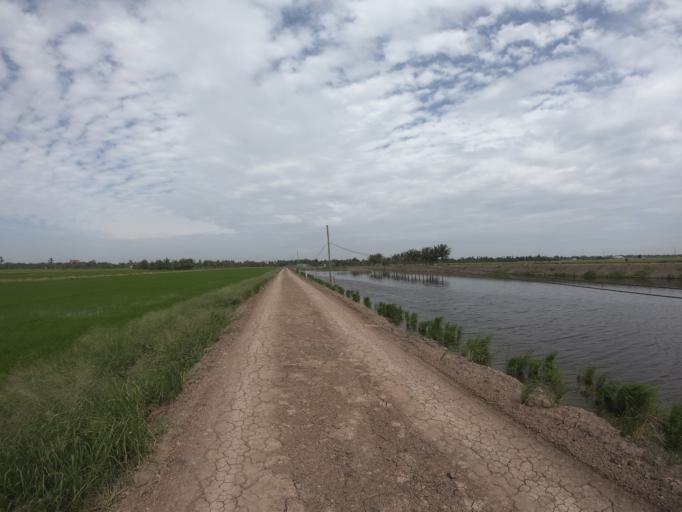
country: TH
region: Pathum Thani
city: Ban Lam Luk Ka
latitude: 14.0247
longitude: 100.8529
